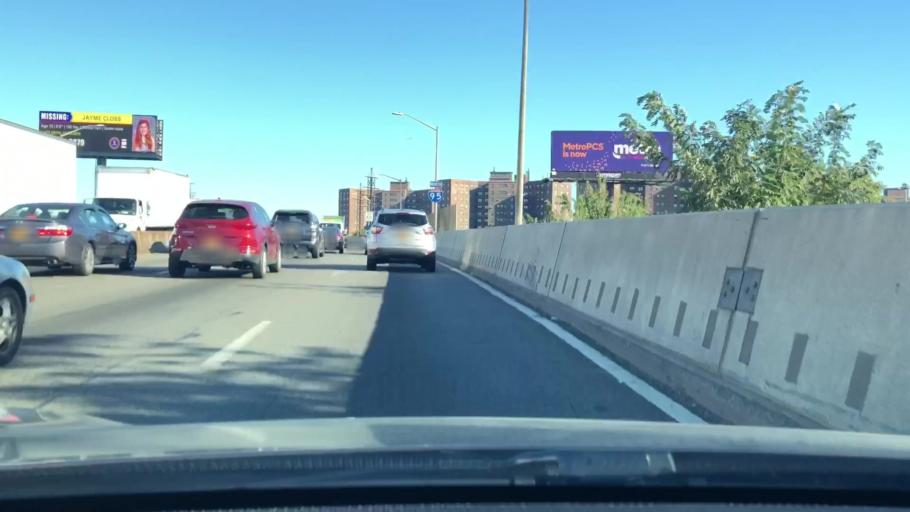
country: US
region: New York
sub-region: Bronx
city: The Bronx
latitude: 40.8371
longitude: -73.8799
